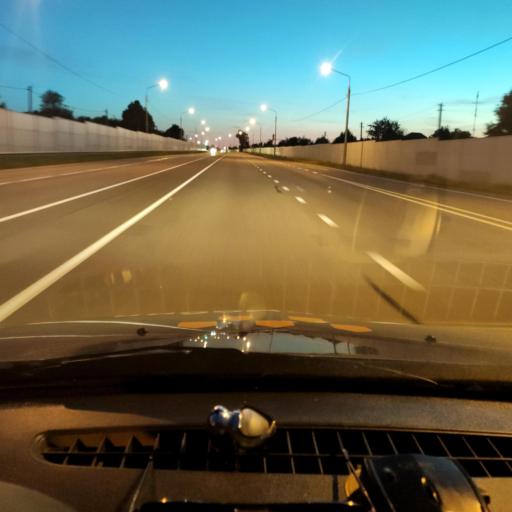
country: RU
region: Belgorod
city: Skorodnoye
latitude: 51.1860
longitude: 37.3797
